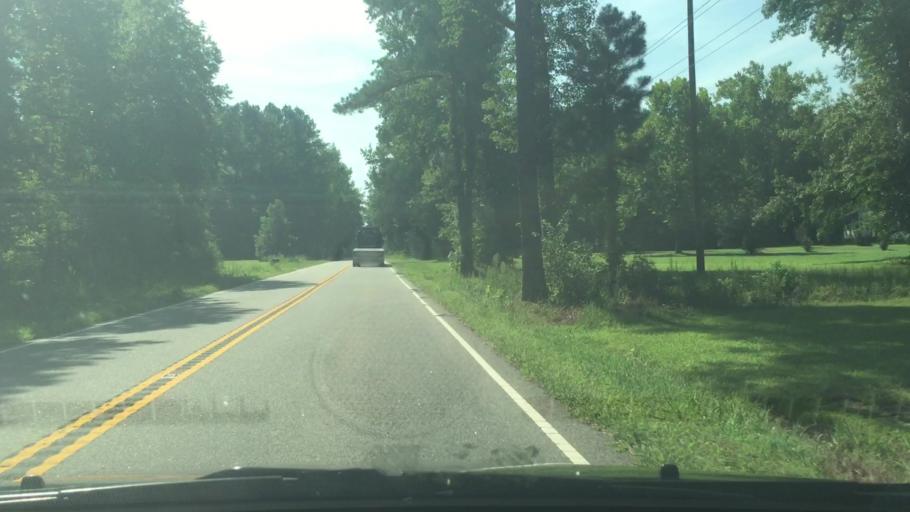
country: US
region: Virginia
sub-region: Sussex County
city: Sussex
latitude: 37.0226
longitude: -77.2886
